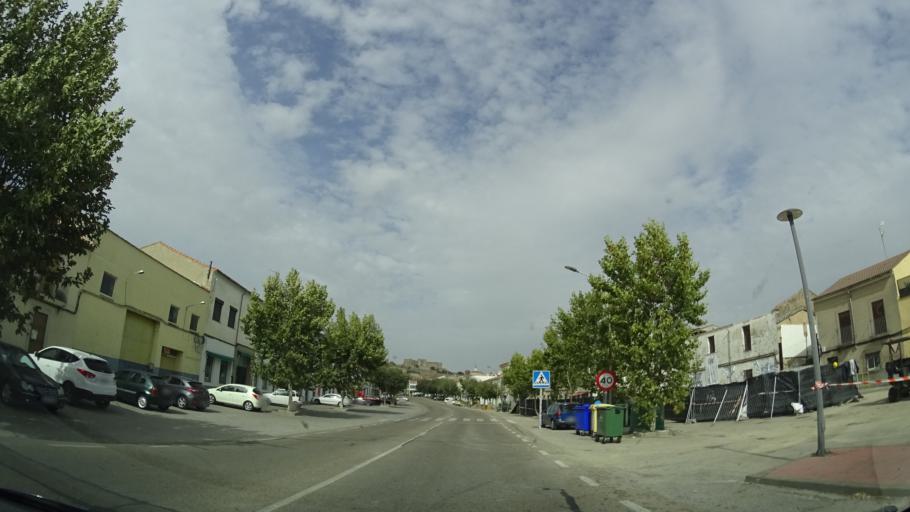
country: ES
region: Extremadura
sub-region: Provincia de Caceres
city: Trujillo
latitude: 39.4534
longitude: -5.8805
